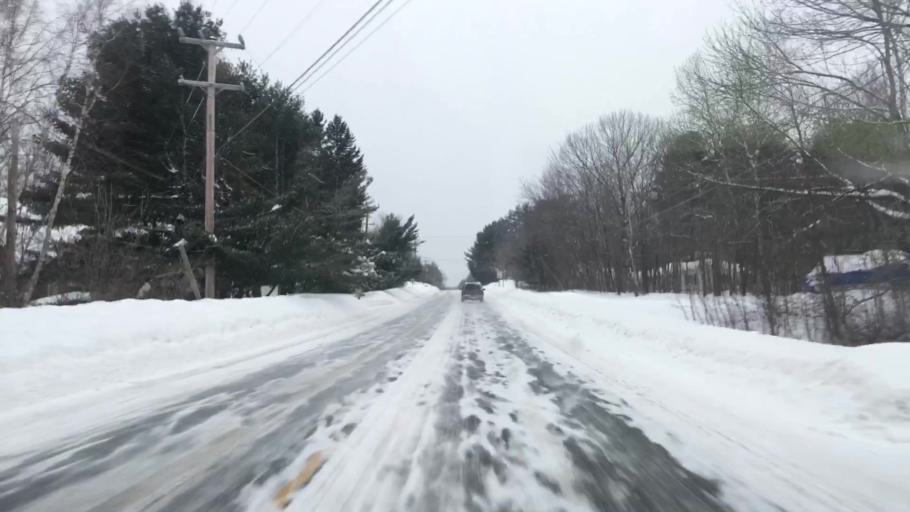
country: US
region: Maine
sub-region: Penobscot County
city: Medway
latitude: 45.5961
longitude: -68.4956
